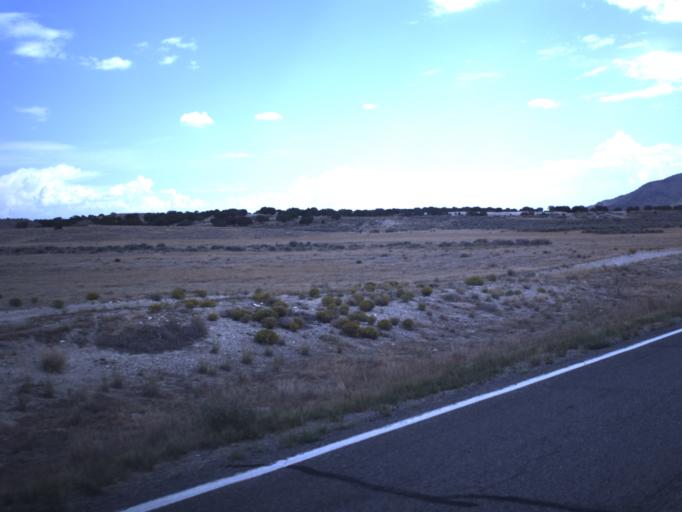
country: US
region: Utah
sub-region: Utah County
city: Eagle Mountain
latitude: 40.2424
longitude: -112.2073
